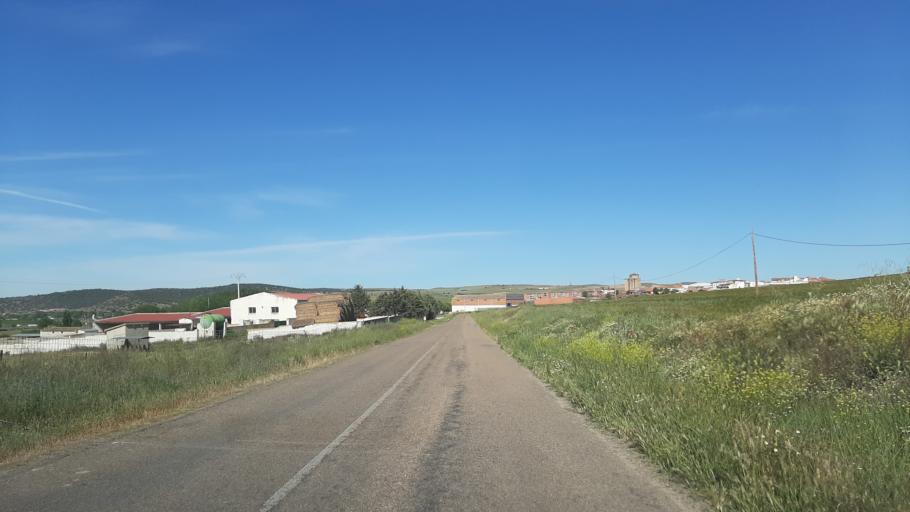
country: ES
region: Castille and Leon
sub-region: Provincia de Salamanca
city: Alba de Tormes
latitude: 40.8204
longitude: -5.5001
